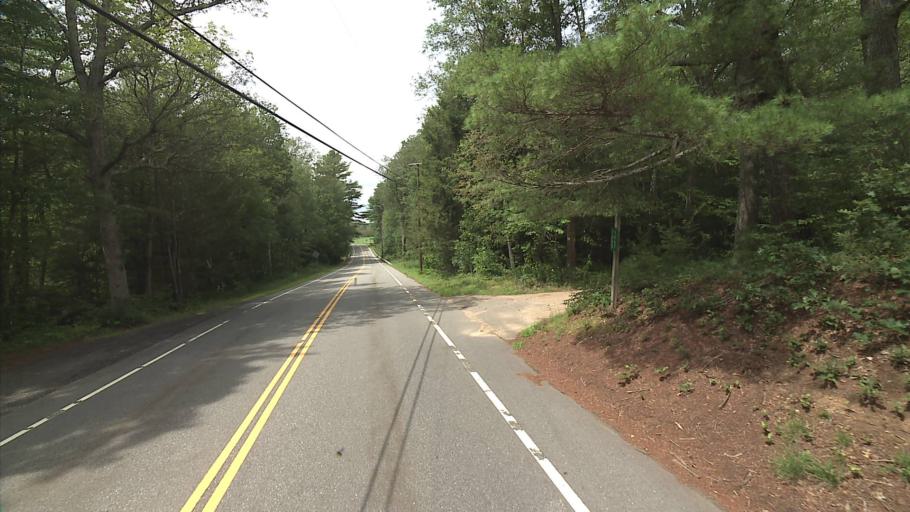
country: US
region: Connecticut
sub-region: Windham County
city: South Woodstock
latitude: 41.9359
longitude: -72.0950
